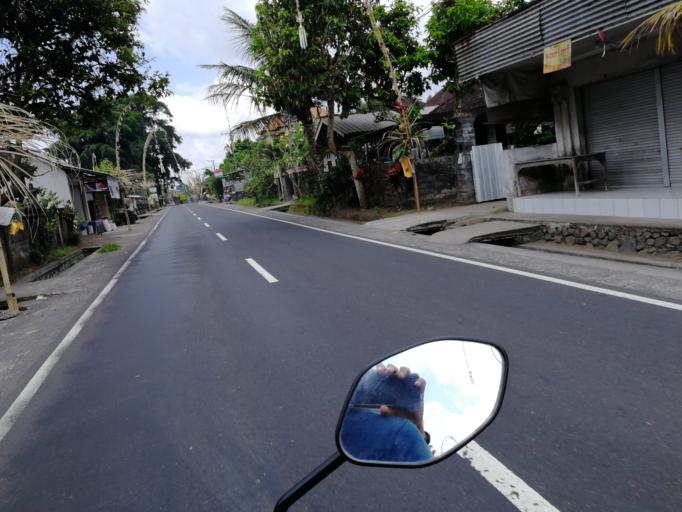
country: ID
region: Bali
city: Banjar Wangsian
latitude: -8.4285
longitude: 115.4306
